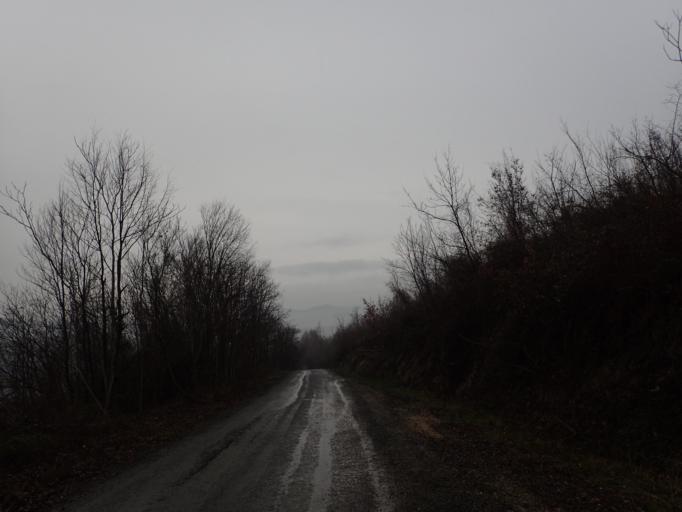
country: TR
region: Ordu
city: Camas
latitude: 40.9480
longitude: 37.5095
